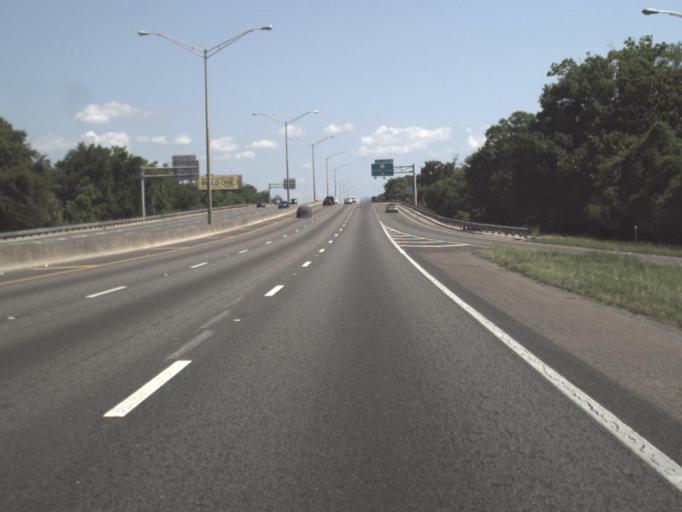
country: US
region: Florida
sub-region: Duval County
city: Jacksonville
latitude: 30.3487
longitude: -81.6683
